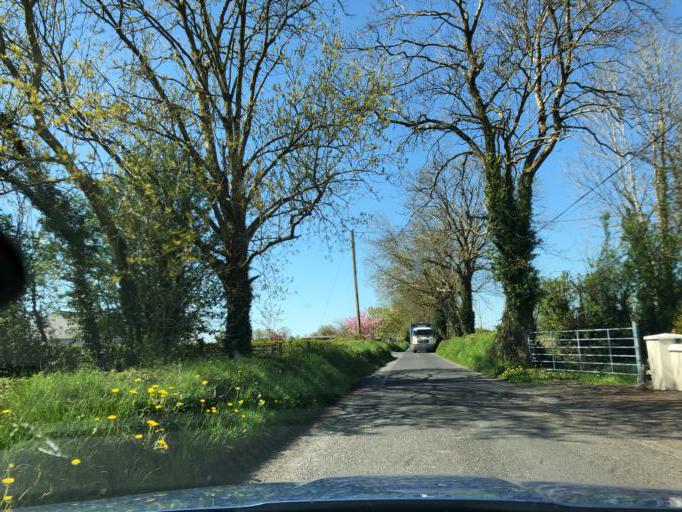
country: IE
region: Connaught
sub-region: County Galway
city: Portumna
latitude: 53.1576
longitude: -8.3062
